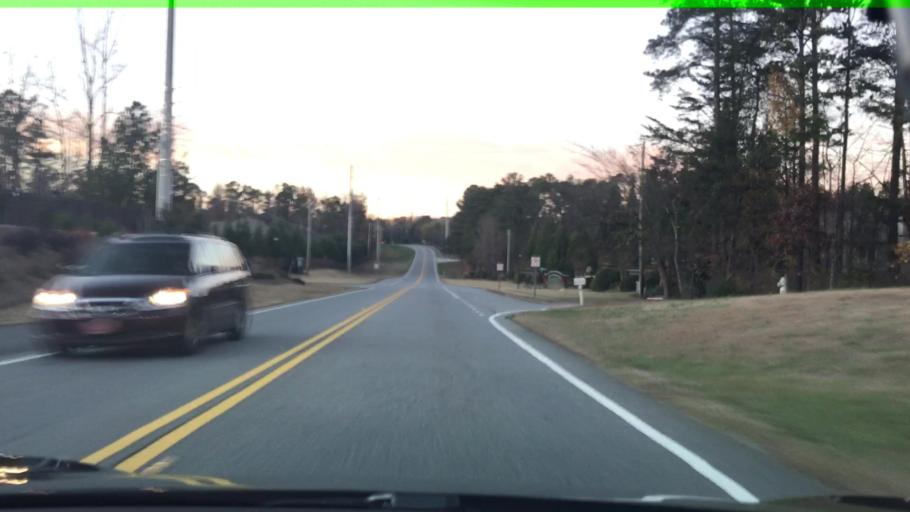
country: US
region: Georgia
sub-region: Gwinnett County
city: Suwanee
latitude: 34.0874
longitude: -84.1323
